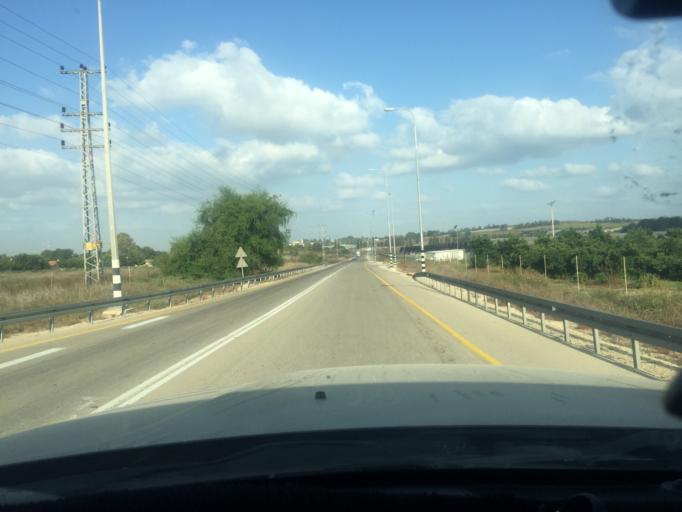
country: PS
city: Umm an Nasr
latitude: 31.6093
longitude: 34.5449
